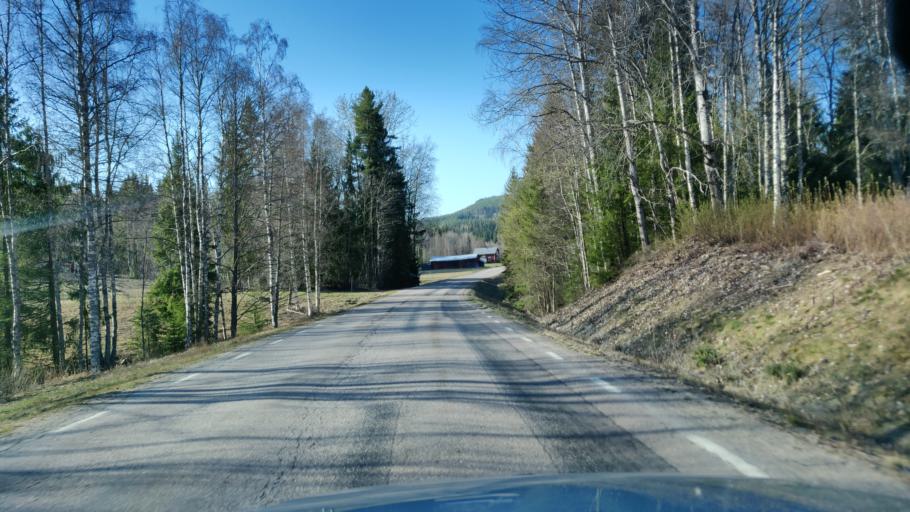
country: SE
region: Vaermland
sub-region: Munkfors Kommun
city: Munkfors
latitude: 59.9734
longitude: 13.4151
